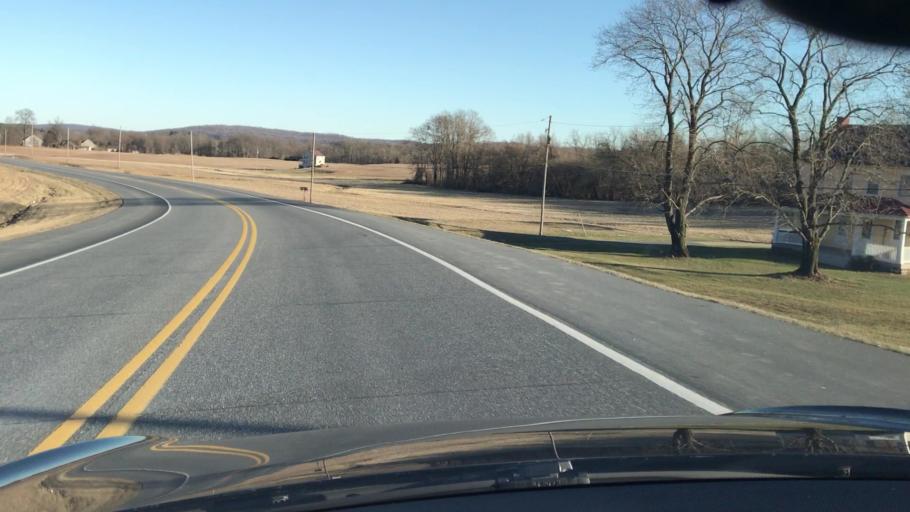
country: US
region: Pennsylvania
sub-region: Cumberland County
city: Lower Allen
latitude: 40.1477
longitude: -76.8827
